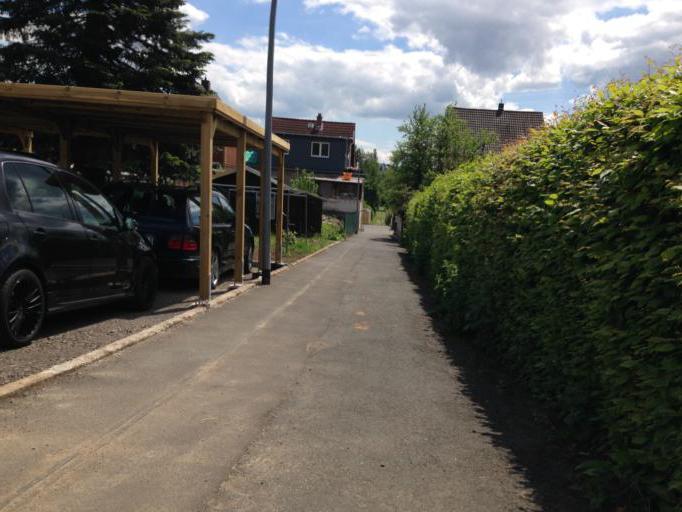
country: DE
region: Hesse
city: Lollar
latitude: 50.6611
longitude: 8.7088
